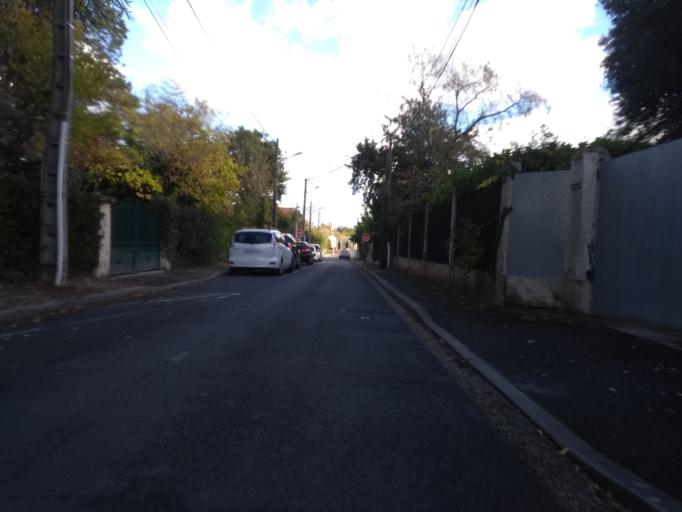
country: FR
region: Aquitaine
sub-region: Departement de la Gironde
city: Pessac
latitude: 44.7996
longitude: -0.6279
